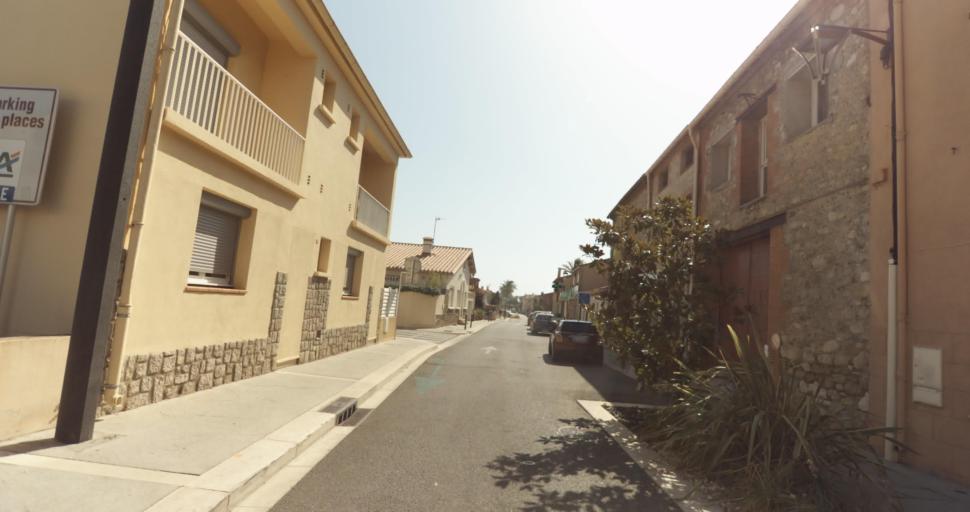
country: FR
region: Languedoc-Roussillon
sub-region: Departement des Pyrenees-Orientales
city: Latour-Bas-Elne
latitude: 42.6182
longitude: 3.0038
